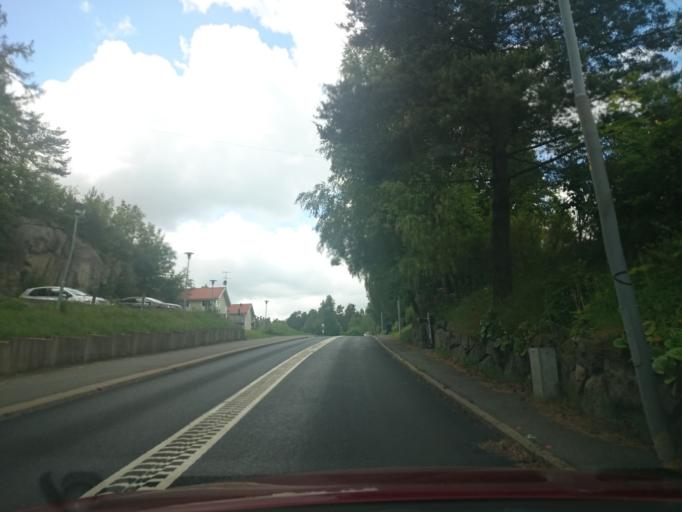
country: SE
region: Vaestra Goetaland
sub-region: Molndal
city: Moelndal
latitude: 57.6684
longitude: 12.0572
